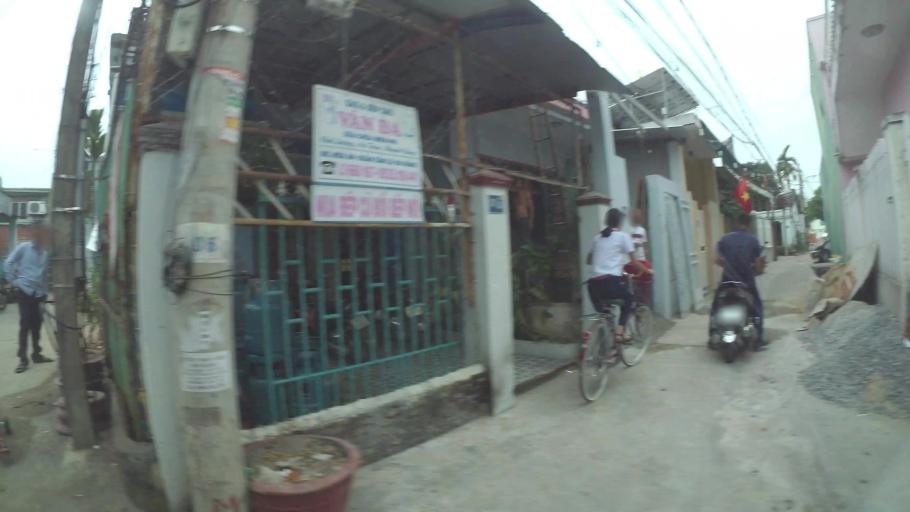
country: VN
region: Da Nang
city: Thanh Khe
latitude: 16.0454
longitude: 108.1806
